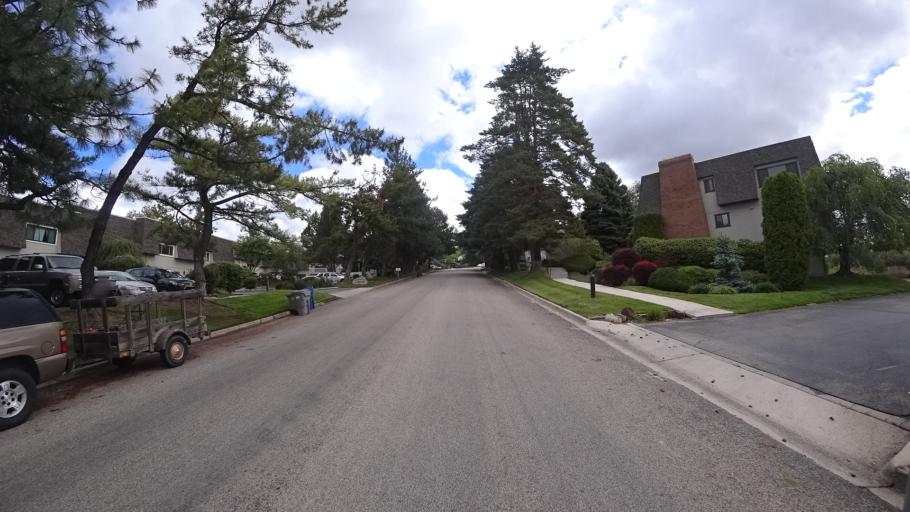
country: US
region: Idaho
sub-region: Ada County
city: Boise
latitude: 43.6491
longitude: -116.1892
